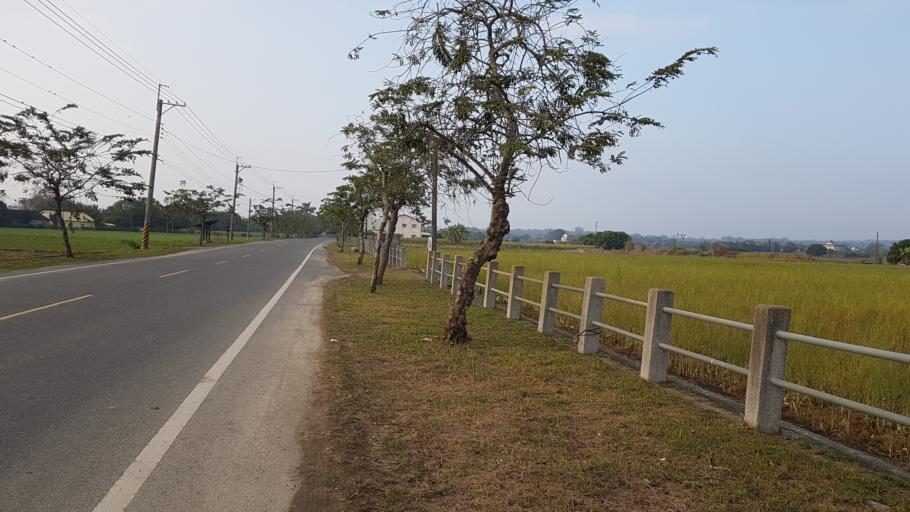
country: TW
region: Taiwan
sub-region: Chiayi
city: Jiayi Shi
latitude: 23.3702
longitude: 120.4504
